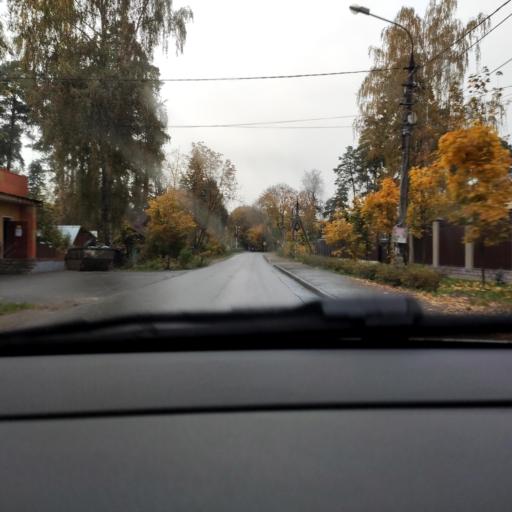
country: RU
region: Moskovskaya
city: Mamontovka
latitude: 55.9783
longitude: 37.8370
